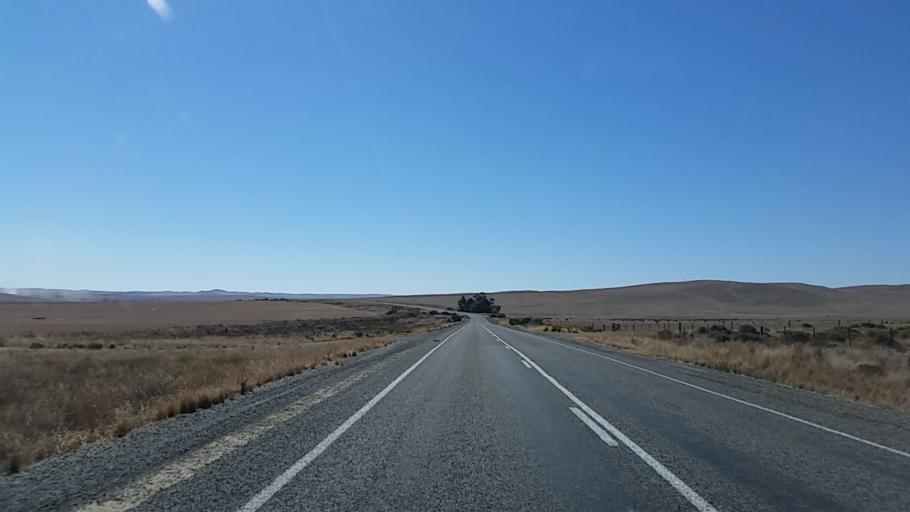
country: AU
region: South Australia
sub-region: Northern Areas
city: Jamestown
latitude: -33.3153
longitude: 138.8827
